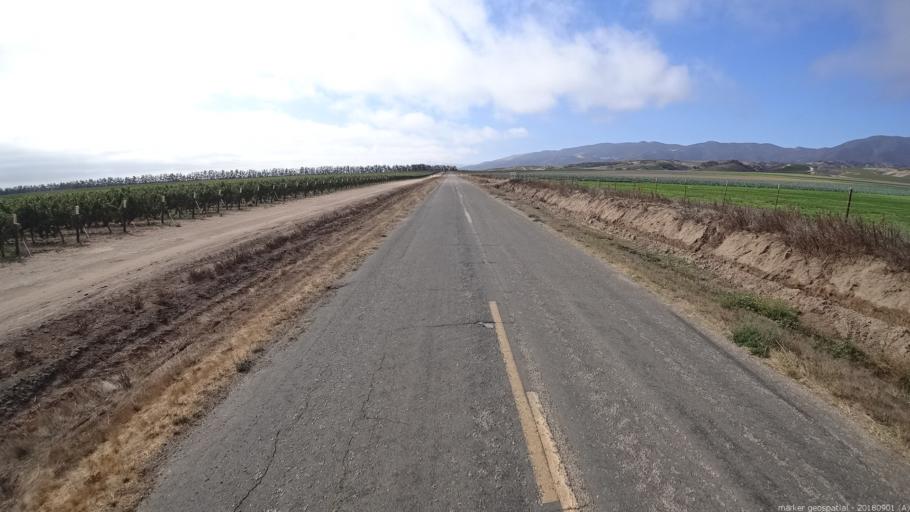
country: US
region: California
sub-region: Monterey County
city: Soledad
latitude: 36.3690
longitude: -121.3364
